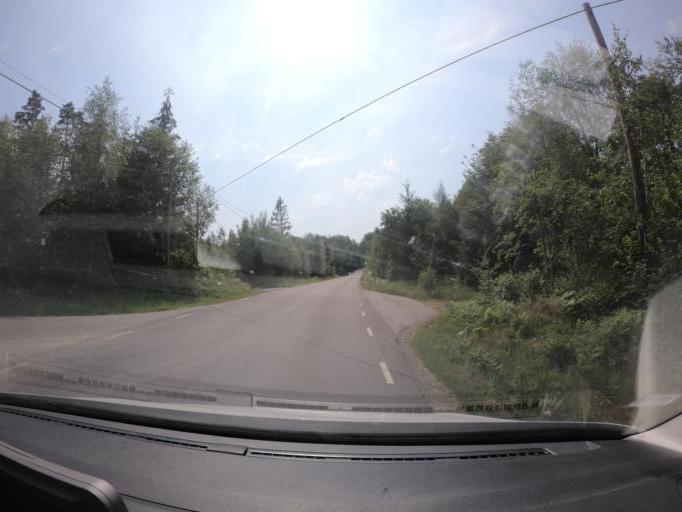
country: SE
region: Skane
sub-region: Hassleholms Kommun
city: Bjarnum
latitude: 56.3310
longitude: 13.6195
